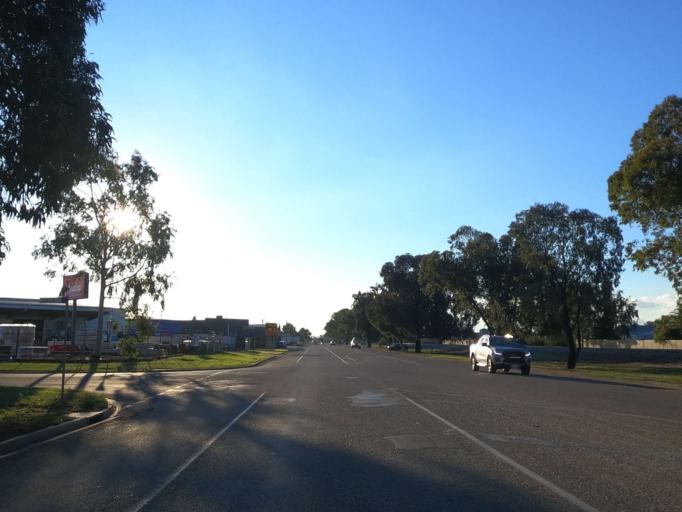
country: AU
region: Victoria
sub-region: Swan Hill
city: Swan Hill
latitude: -35.3321
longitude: 143.5578
